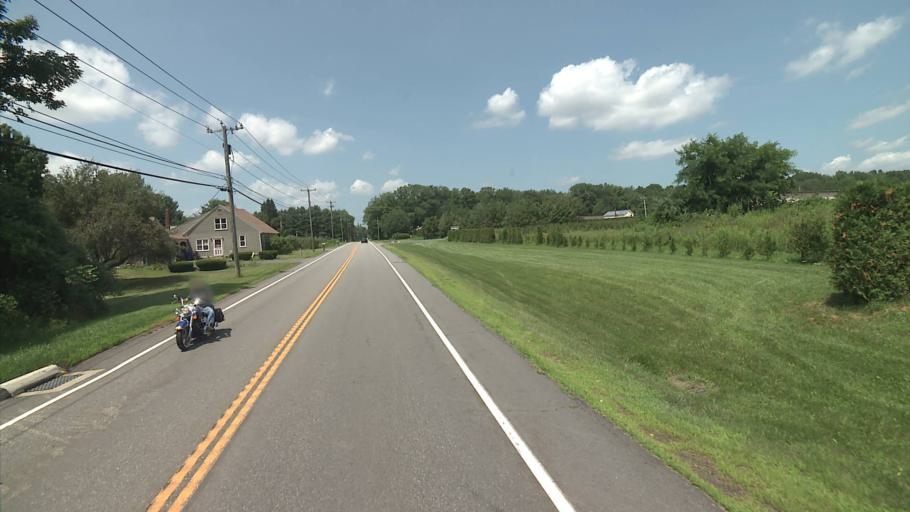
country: US
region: Connecticut
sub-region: Tolland County
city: Tolland
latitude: 41.8167
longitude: -72.3968
